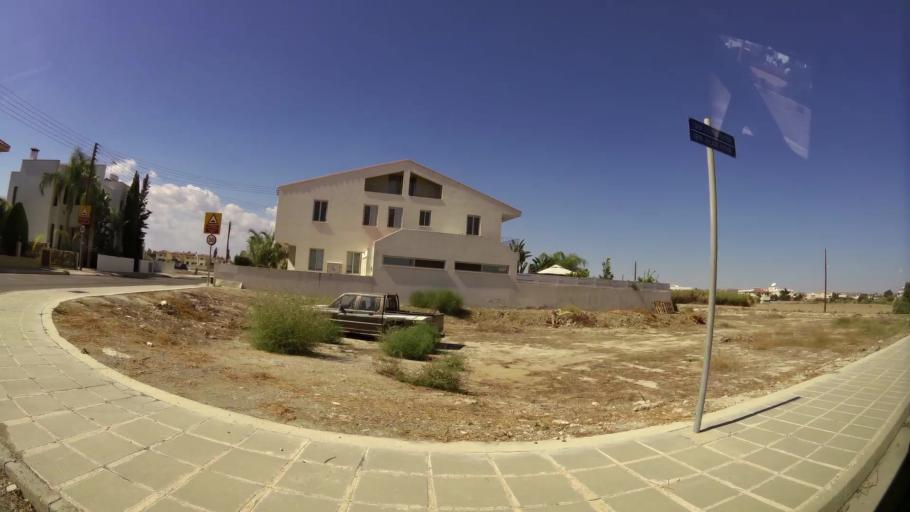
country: CY
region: Larnaka
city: Livadia
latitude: 34.9526
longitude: 33.6346
